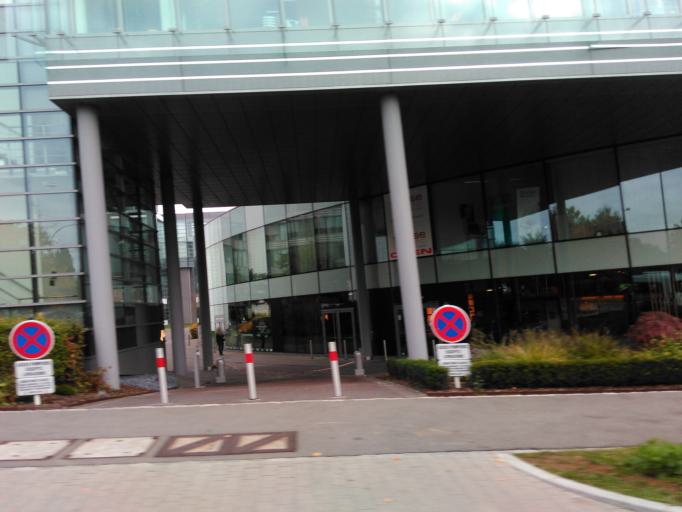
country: LU
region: Luxembourg
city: Kirchberg
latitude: 49.6266
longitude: 6.1612
